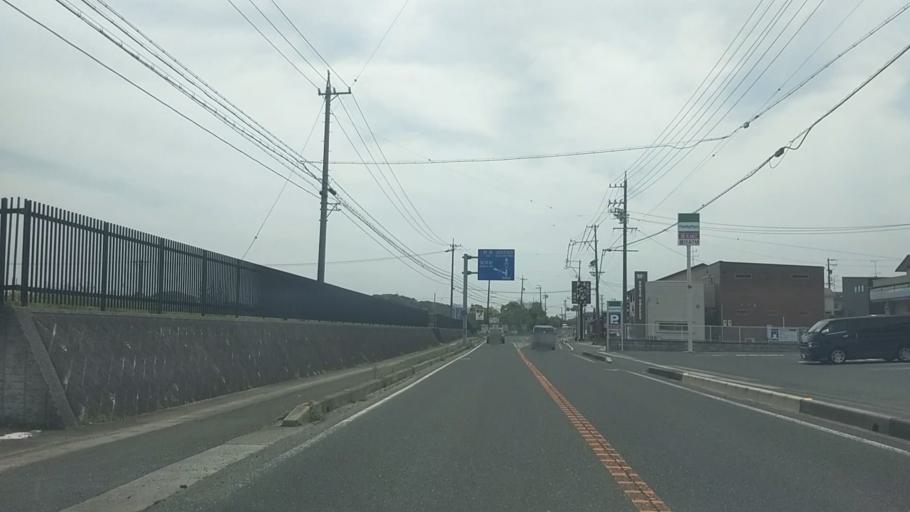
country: JP
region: Shizuoka
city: Kosai-shi
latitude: 34.7257
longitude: 137.5271
